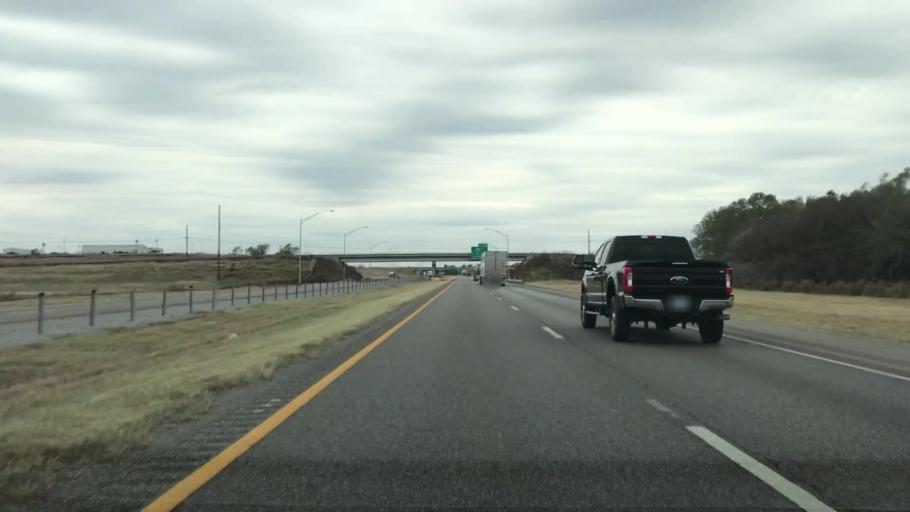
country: US
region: Oklahoma
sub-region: Custer County
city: Clinton
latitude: 35.5002
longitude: -98.9564
